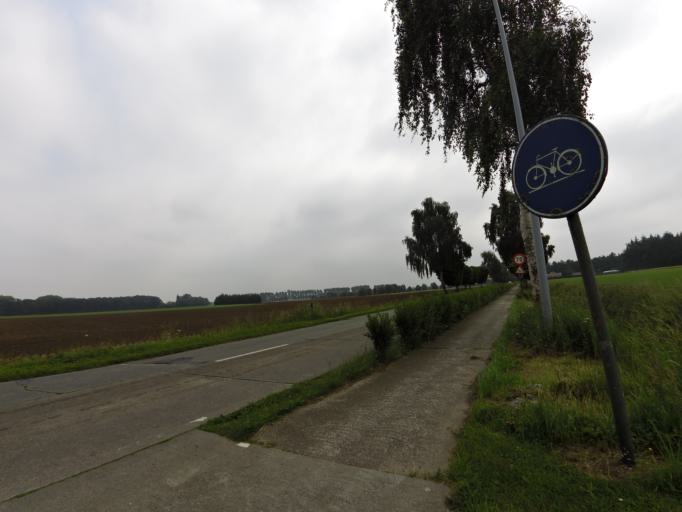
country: BE
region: Flanders
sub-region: Provincie West-Vlaanderen
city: Jabbeke
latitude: 51.1489
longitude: 3.0852
